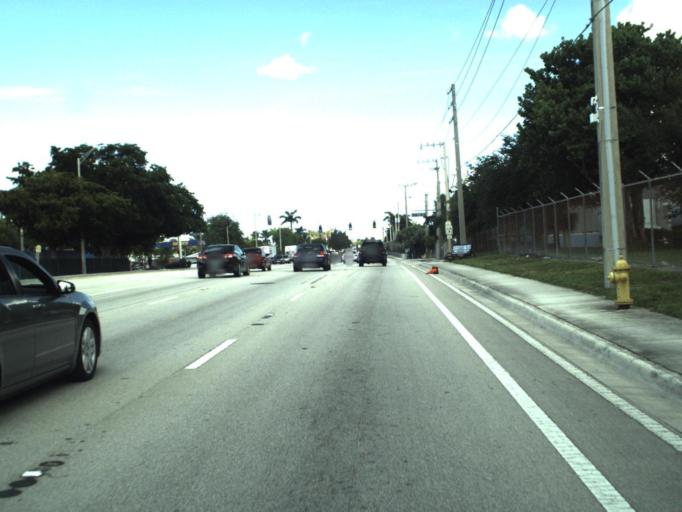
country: US
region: Florida
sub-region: Broward County
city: Pembroke Park
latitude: 25.9955
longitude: -80.1785
